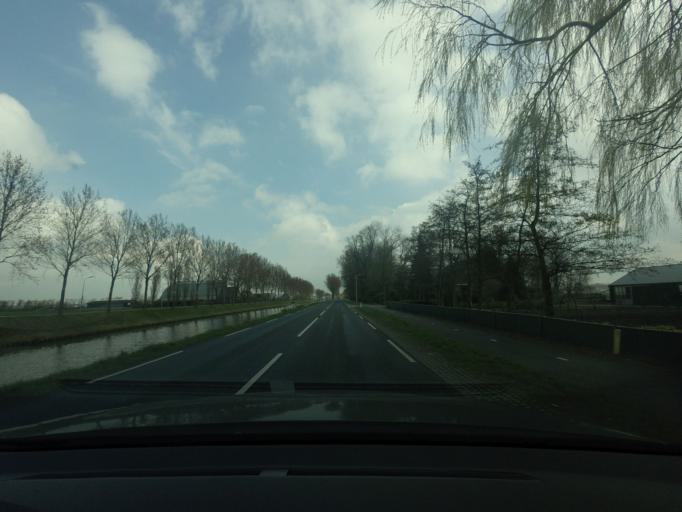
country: NL
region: North Holland
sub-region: Gemeente Haarlemmermeer
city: Hoofddorp
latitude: 52.3430
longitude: 4.7469
